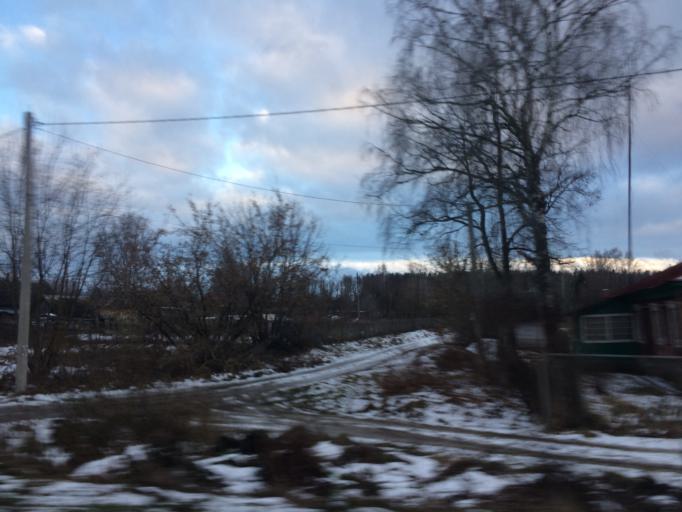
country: RU
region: Tula
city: Cherepet'
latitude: 54.1188
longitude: 36.3850
